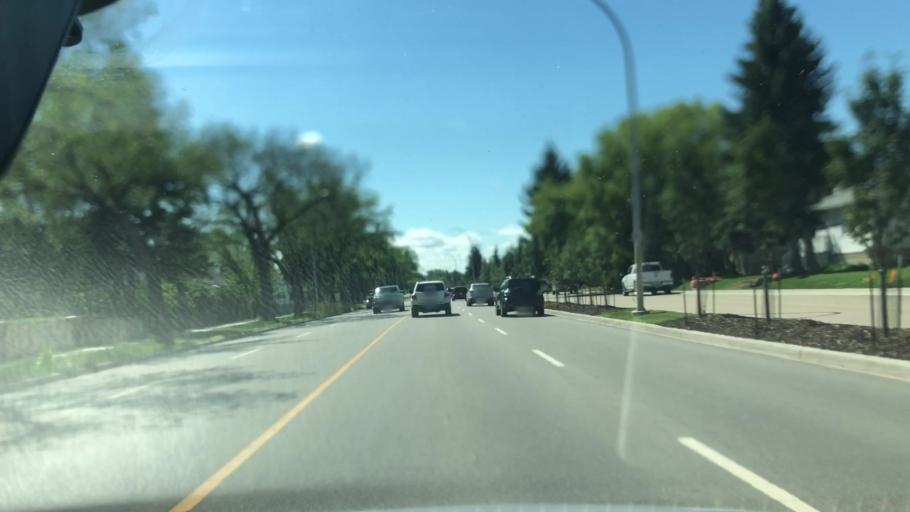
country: CA
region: Alberta
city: Edmonton
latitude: 53.5748
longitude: -113.5413
